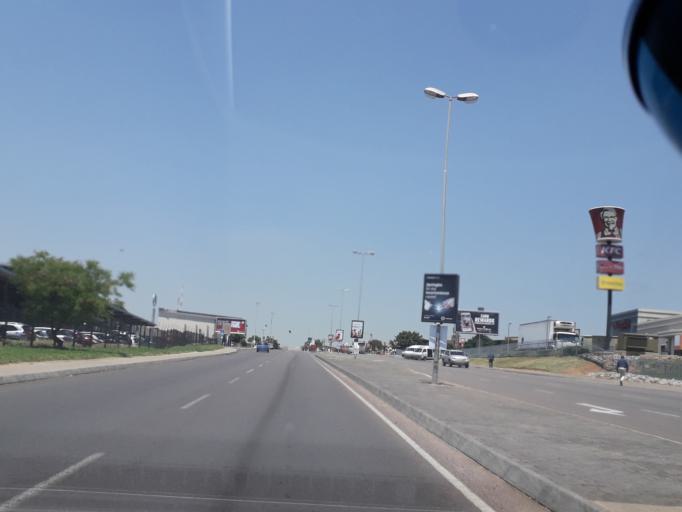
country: ZA
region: Gauteng
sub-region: City of Johannesburg Metropolitan Municipality
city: Midrand
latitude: -25.9765
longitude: 28.1190
